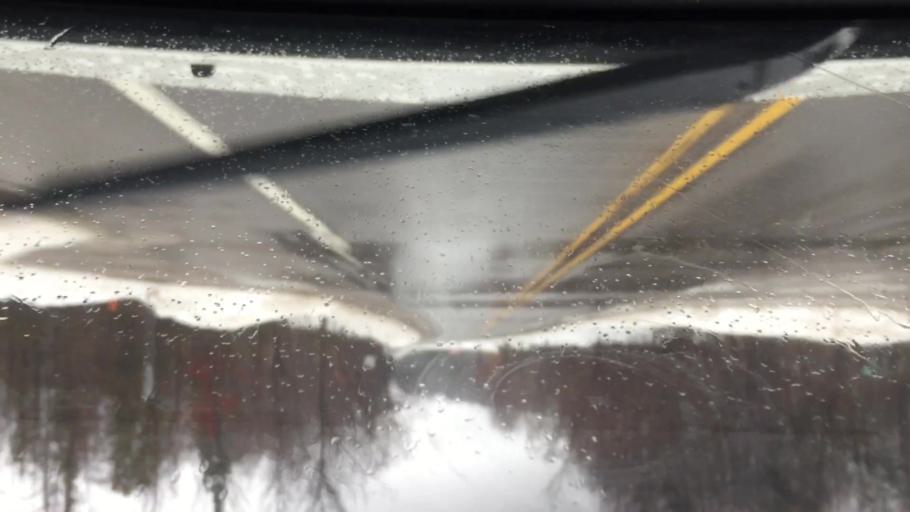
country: US
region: Michigan
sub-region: Charlevoix County
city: East Jordan
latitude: 45.1973
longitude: -85.1651
